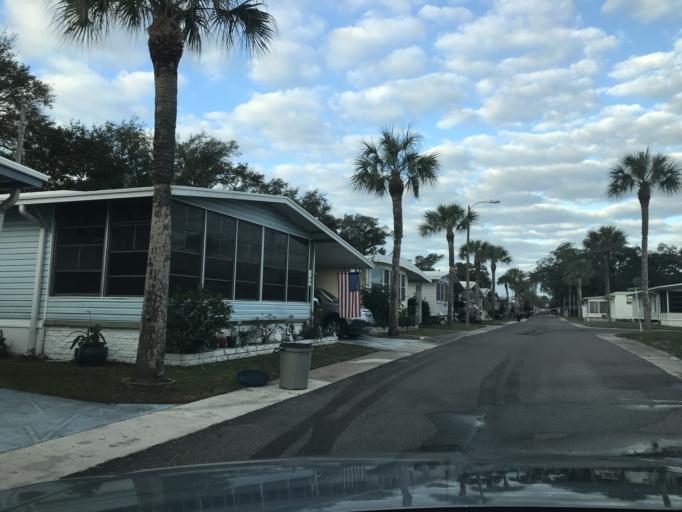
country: US
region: Florida
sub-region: Pinellas County
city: Largo
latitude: 27.9216
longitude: -82.7838
